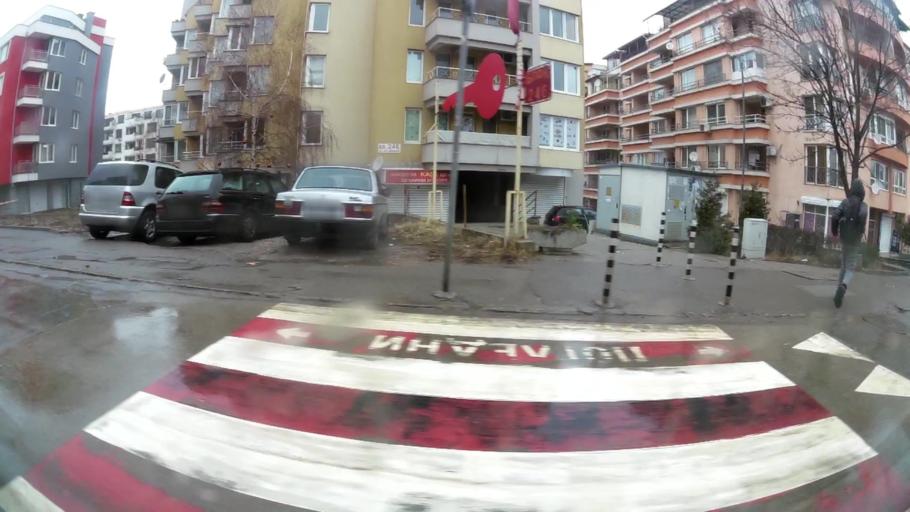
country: BG
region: Sofia-Capital
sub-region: Stolichna Obshtina
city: Sofia
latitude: 42.6445
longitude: 23.3670
